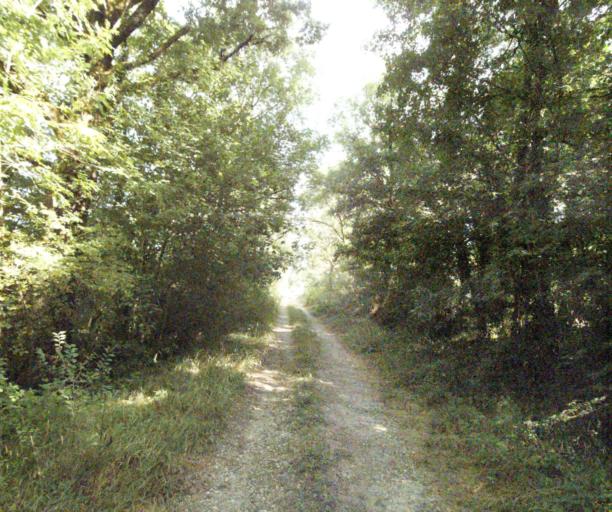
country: FR
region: Midi-Pyrenees
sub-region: Departement du Tarn
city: Soual
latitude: 43.5233
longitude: 2.0943
